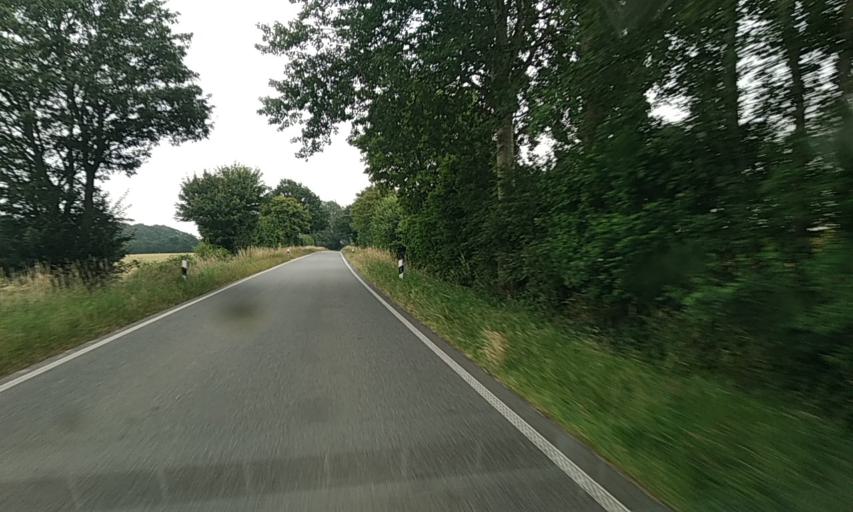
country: DE
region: Schleswig-Holstein
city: Loit
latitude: 54.6089
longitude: 9.7143
